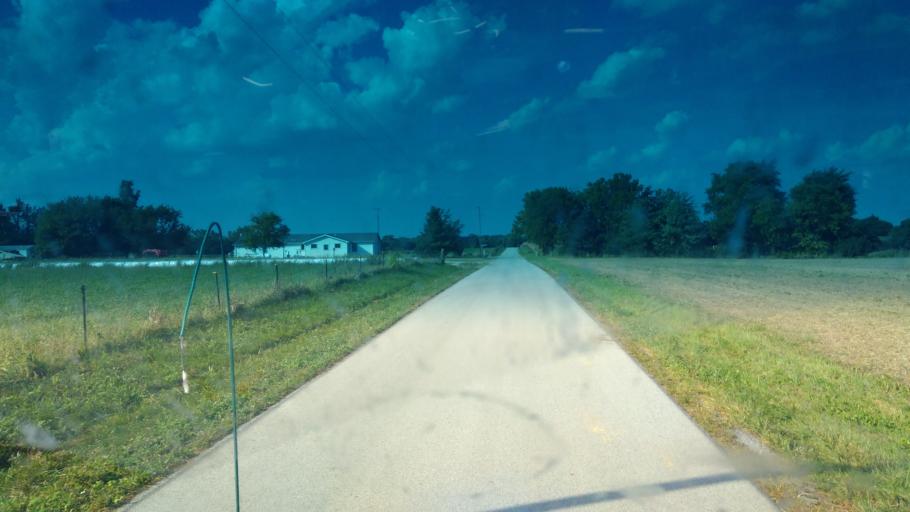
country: US
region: Ohio
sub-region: Hancock County
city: Arlington
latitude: 40.8716
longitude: -83.5854
